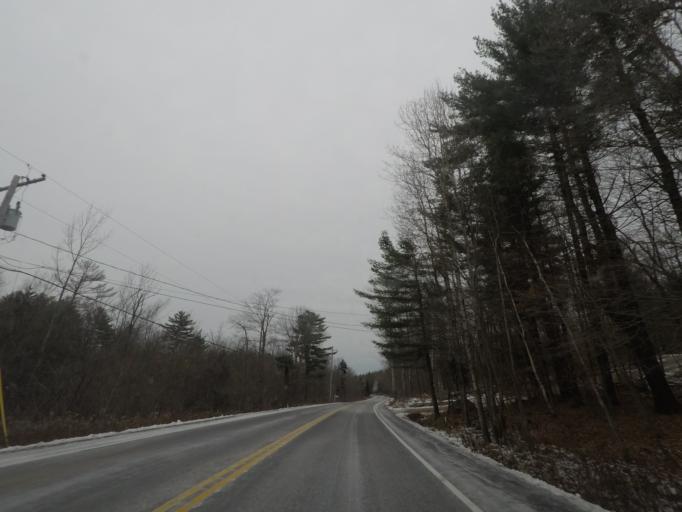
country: US
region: New York
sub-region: Rensselaer County
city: Hoosick Falls
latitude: 42.7662
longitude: -73.4052
